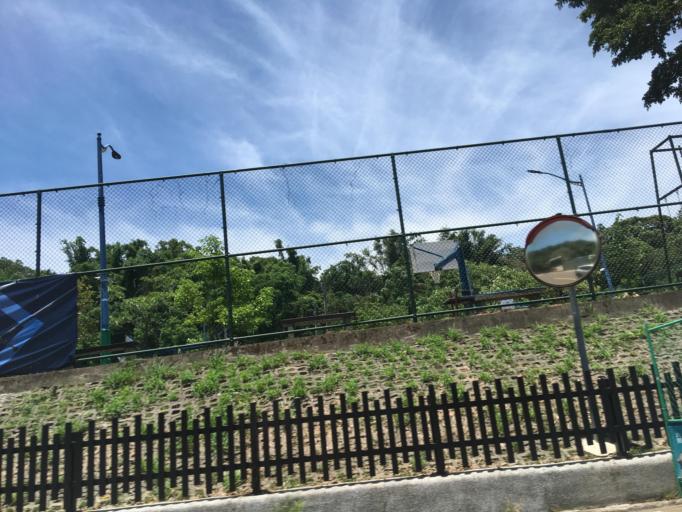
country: TW
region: Taipei
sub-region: Taipei
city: Banqiao
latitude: 25.0551
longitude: 121.4273
